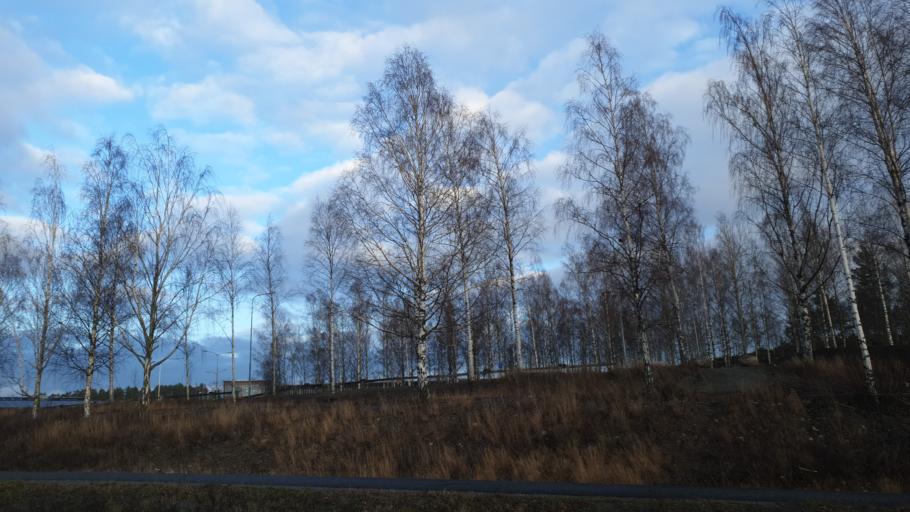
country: SE
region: Gaevleborg
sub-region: Hudiksvalls Kommun
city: Hudiksvall
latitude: 61.7226
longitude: 17.1264
